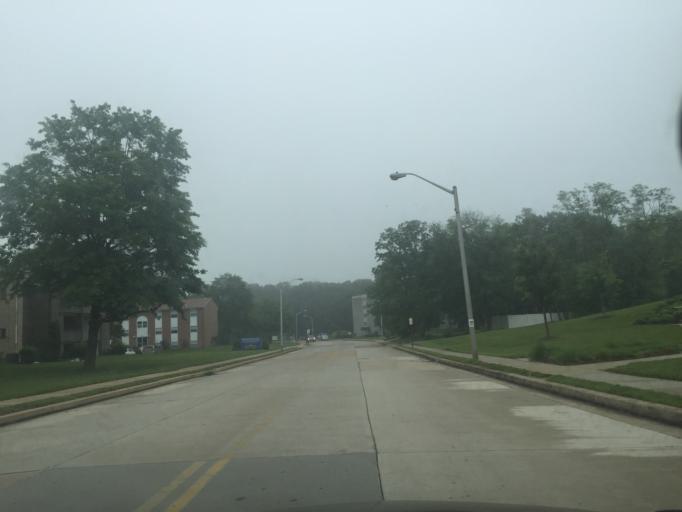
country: US
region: Maryland
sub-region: Baltimore County
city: Pikesville
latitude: 39.3702
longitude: -76.6884
